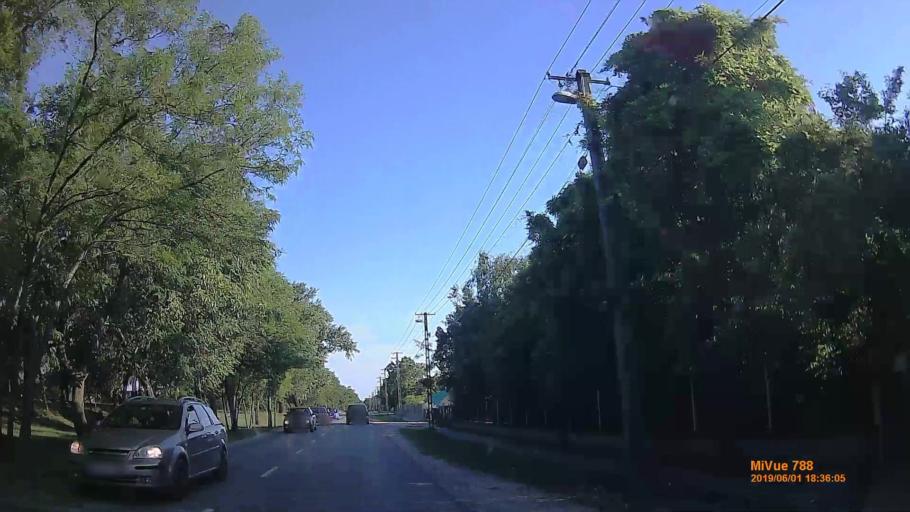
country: HU
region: Pest
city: Dunavarsany
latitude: 47.2860
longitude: 19.0671
